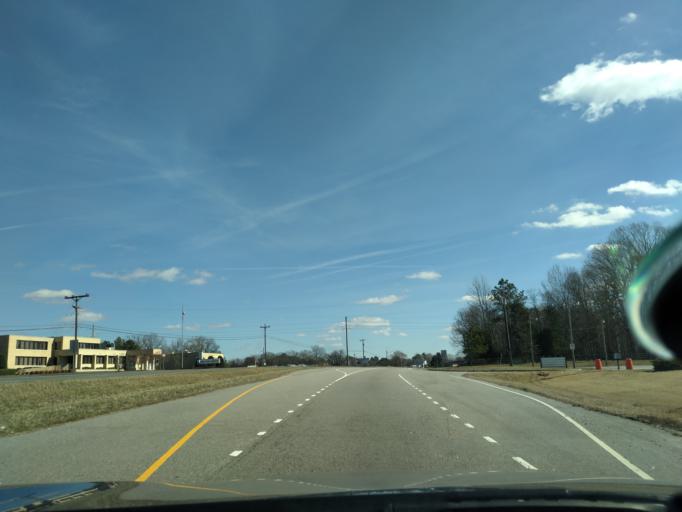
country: US
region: Virginia
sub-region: Nottoway County
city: Crewe
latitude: 37.1903
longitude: -78.1494
